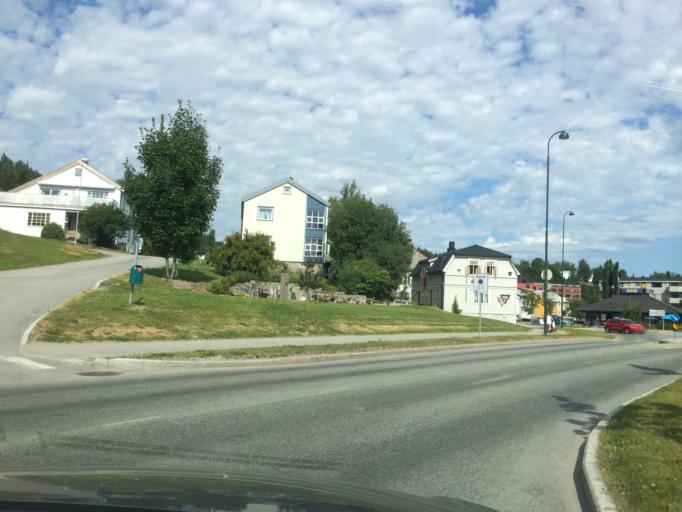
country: NO
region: Nord-Trondelag
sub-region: Namsos
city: Namsos
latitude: 64.4682
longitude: 11.4997
